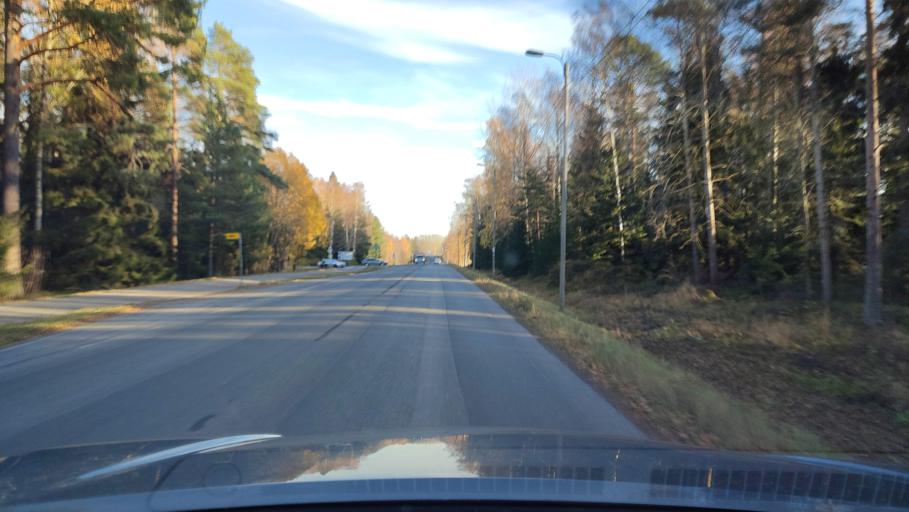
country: FI
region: Ostrobothnia
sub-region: Vaasa
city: Teeriniemi
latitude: 63.0770
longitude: 21.6745
